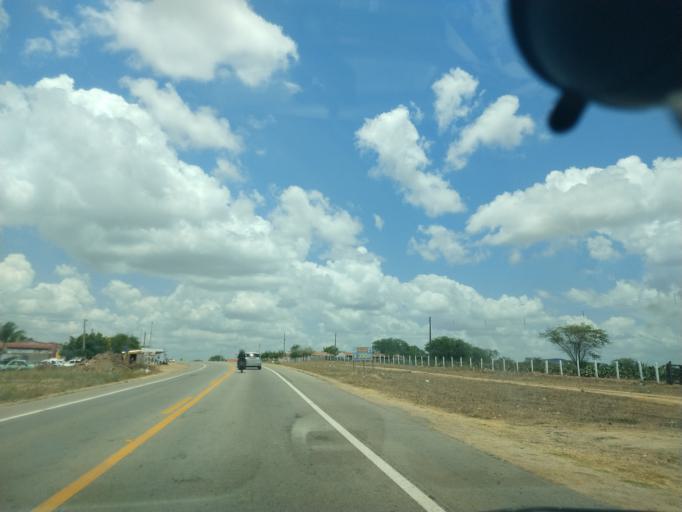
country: BR
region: Rio Grande do Norte
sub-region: Tangara
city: Tangara
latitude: -6.1895
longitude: -35.7863
